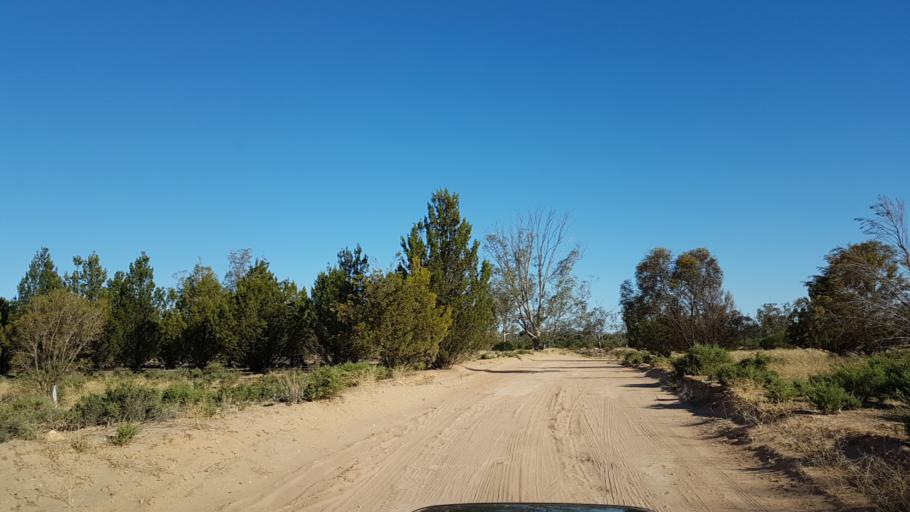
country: AU
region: South Australia
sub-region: Loxton Waikerie
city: Waikerie
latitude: -34.1551
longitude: 140.0215
